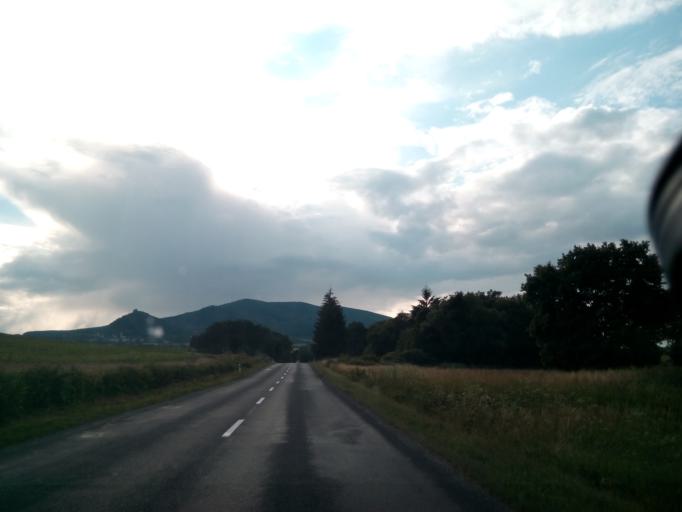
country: SK
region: Kosicky
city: Secovce
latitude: 48.6322
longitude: 21.5151
